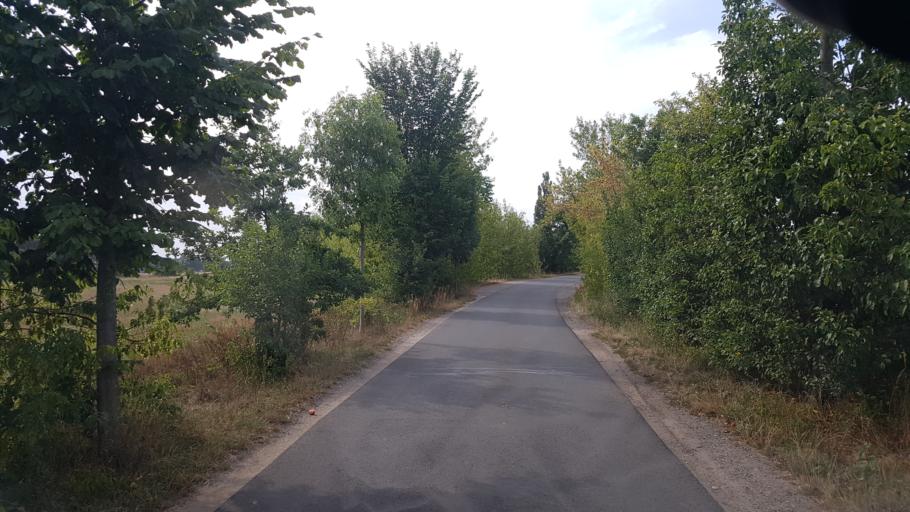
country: DE
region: Brandenburg
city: Elsterwerda
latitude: 51.4415
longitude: 13.5530
